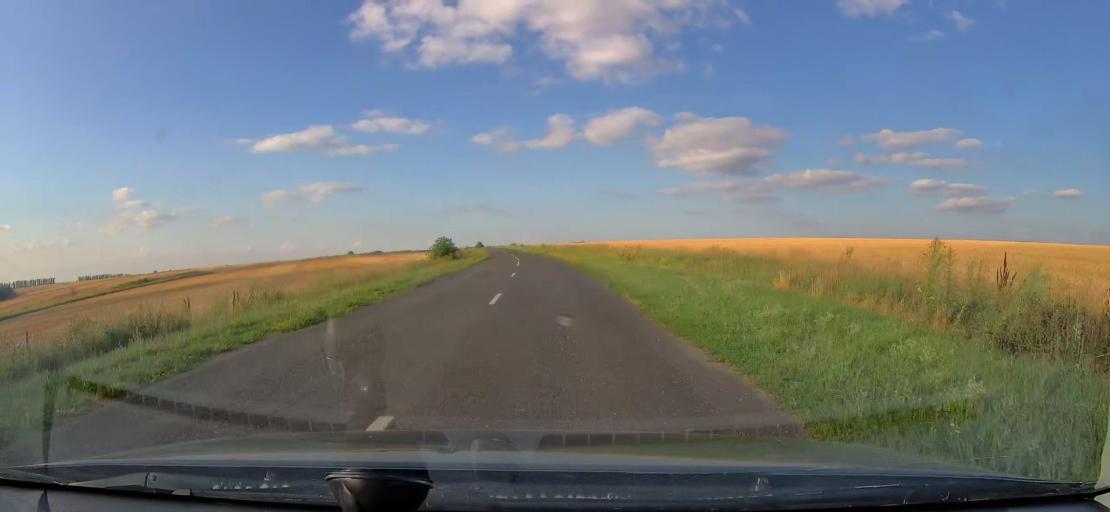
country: RU
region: Kursk
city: Zolotukhino
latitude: 52.0304
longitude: 36.2163
